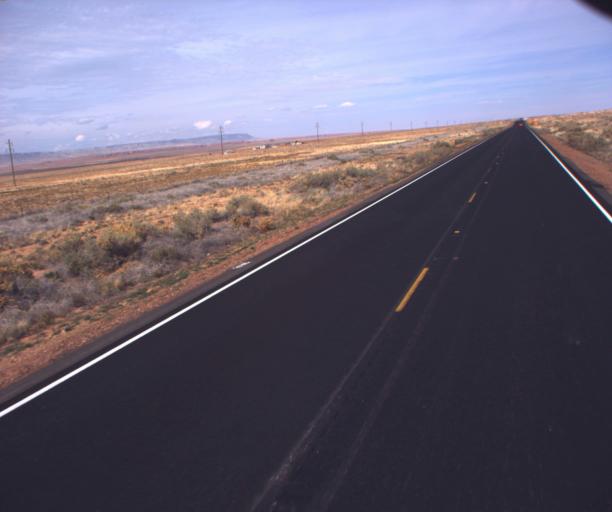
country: US
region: Arizona
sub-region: Apache County
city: Chinle
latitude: 36.0416
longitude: -109.6074
